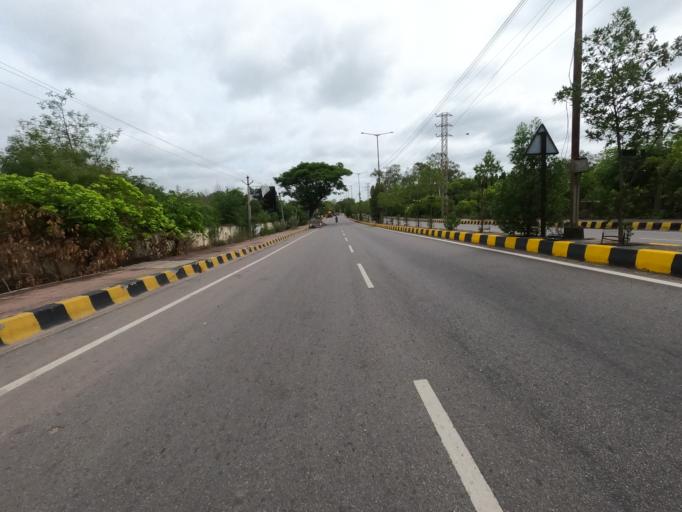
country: IN
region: Telangana
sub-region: Hyderabad
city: Hyderabad
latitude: 17.3323
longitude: 78.4095
